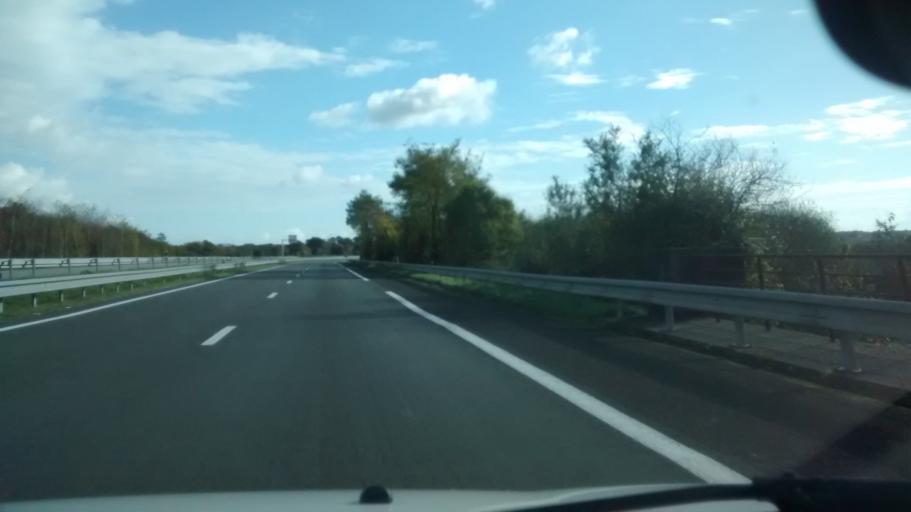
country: FR
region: Pays de la Loire
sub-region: Departement de Maine-et-Loire
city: Pouance
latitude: 47.7566
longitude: -1.1705
